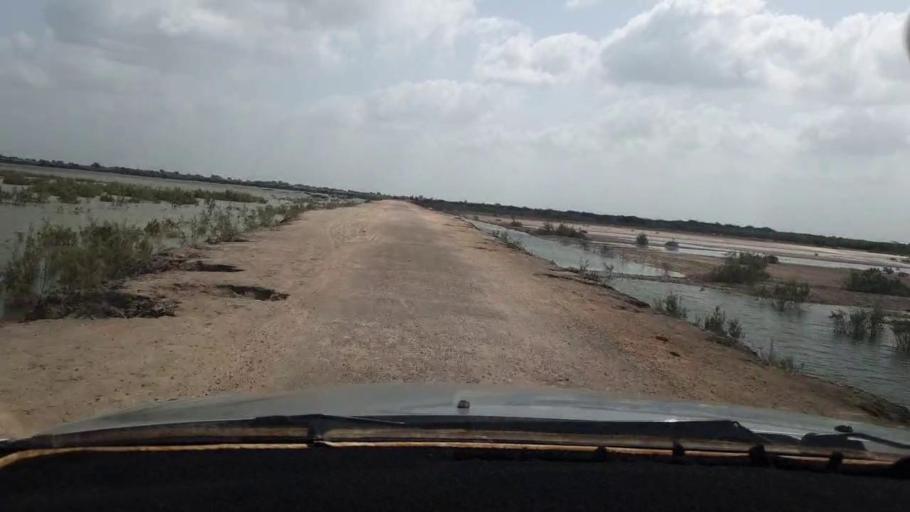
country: PK
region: Sindh
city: Tando Bago
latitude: 24.7207
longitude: 69.1527
